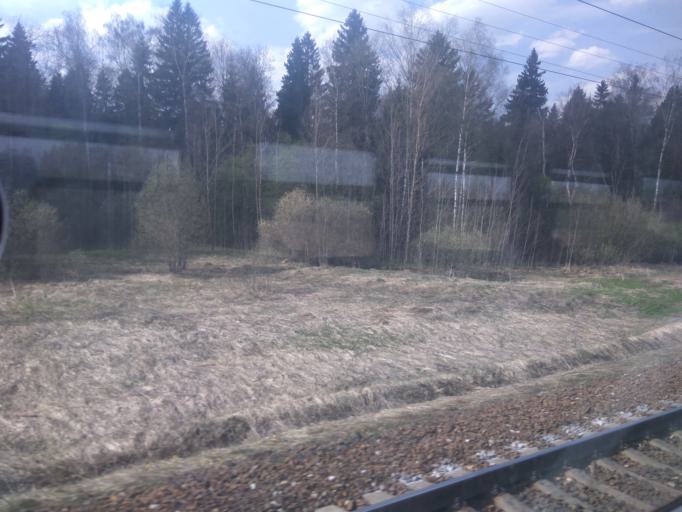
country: RU
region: Moskovskaya
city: Podosinki
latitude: 56.2190
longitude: 37.5272
